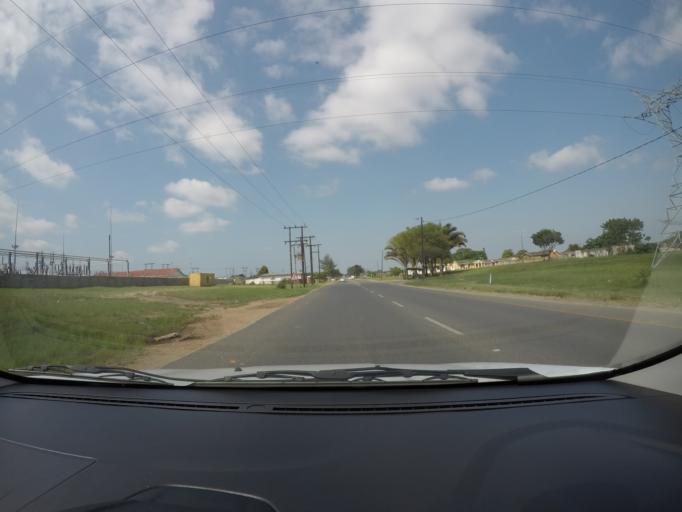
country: ZA
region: KwaZulu-Natal
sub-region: uThungulu District Municipality
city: eSikhawini
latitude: -28.8852
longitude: 31.9006
